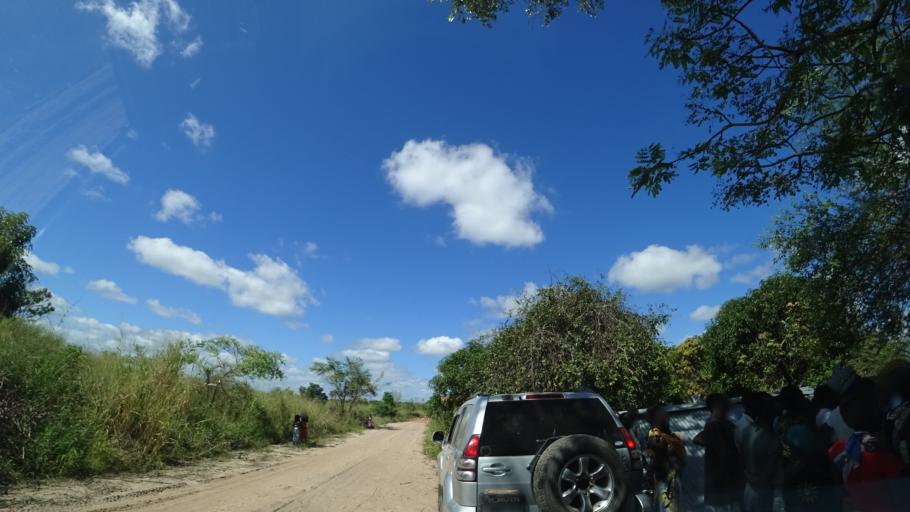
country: MZ
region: Sofala
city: Dondo
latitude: -19.2737
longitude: 34.6801
